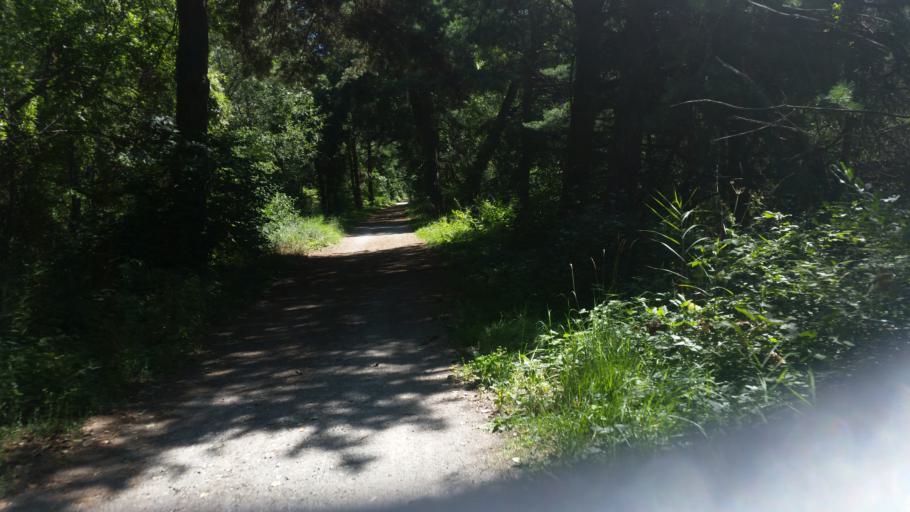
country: CH
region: Valais
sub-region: Leuk District
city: Gampel
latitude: 46.3082
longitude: 7.7688
